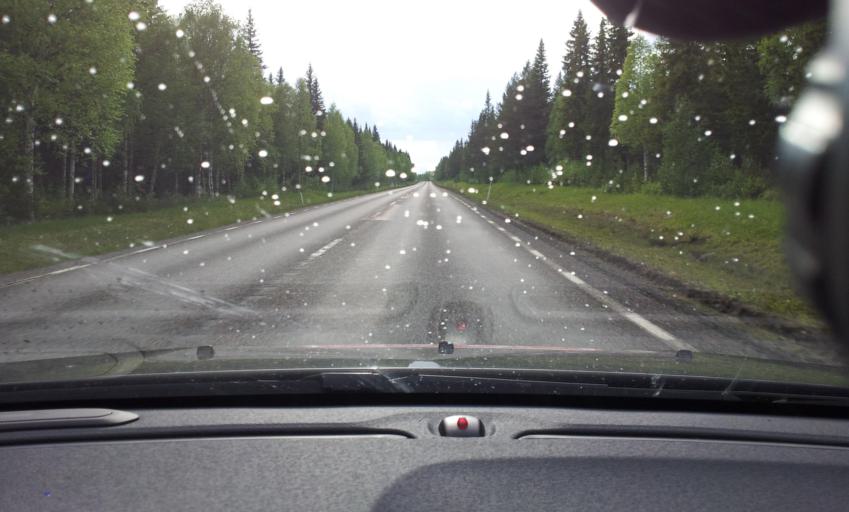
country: SE
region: Jaemtland
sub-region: OEstersunds Kommun
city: Lit
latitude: 63.2035
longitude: 14.9077
